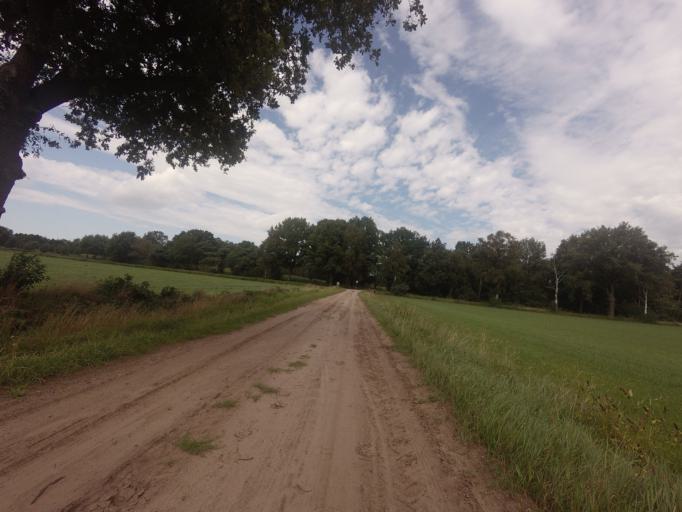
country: NL
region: Overijssel
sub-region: Gemeente Dalfsen
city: Dalfsen
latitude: 52.4849
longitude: 6.3742
